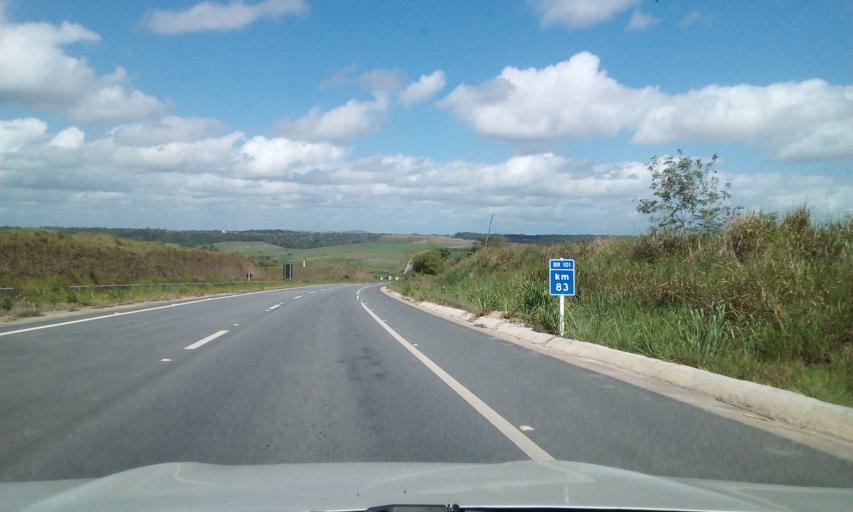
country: BR
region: Alagoas
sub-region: Rio Largo
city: Rio Largo
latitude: -9.4520
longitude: -35.8721
